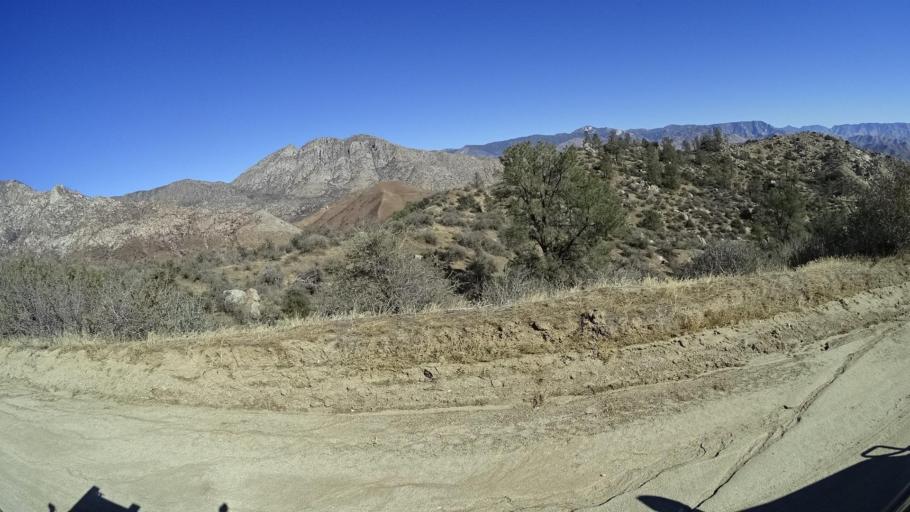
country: US
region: California
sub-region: Kern County
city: Wofford Heights
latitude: 35.7068
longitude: -118.5020
